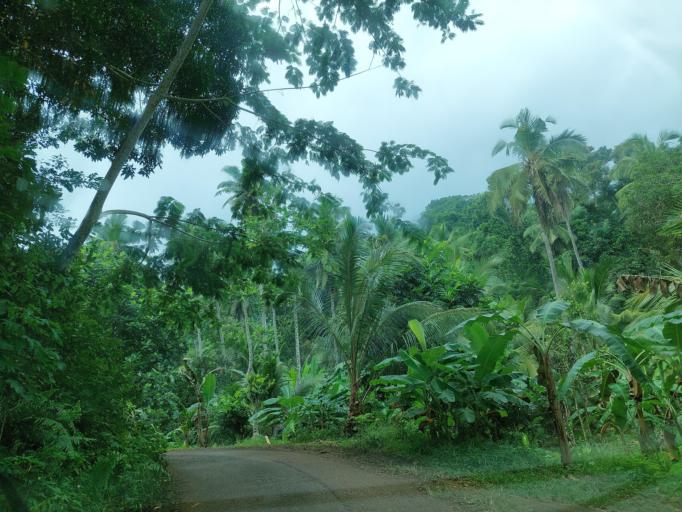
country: YT
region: Tsingoni
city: Tsingoni
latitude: -12.7684
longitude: 45.1146
